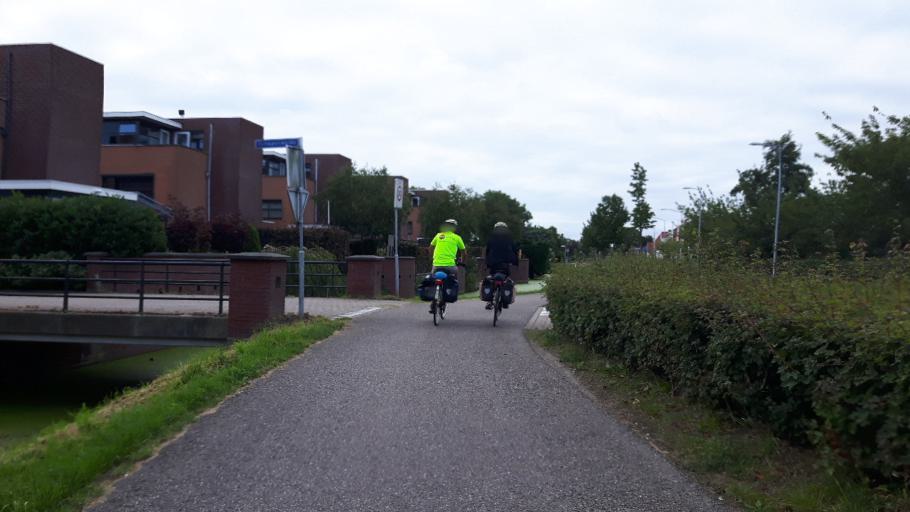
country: NL
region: North Holland
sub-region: Gemeente Hoorn
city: Hoorn
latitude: 52.6607
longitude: 5.0422
